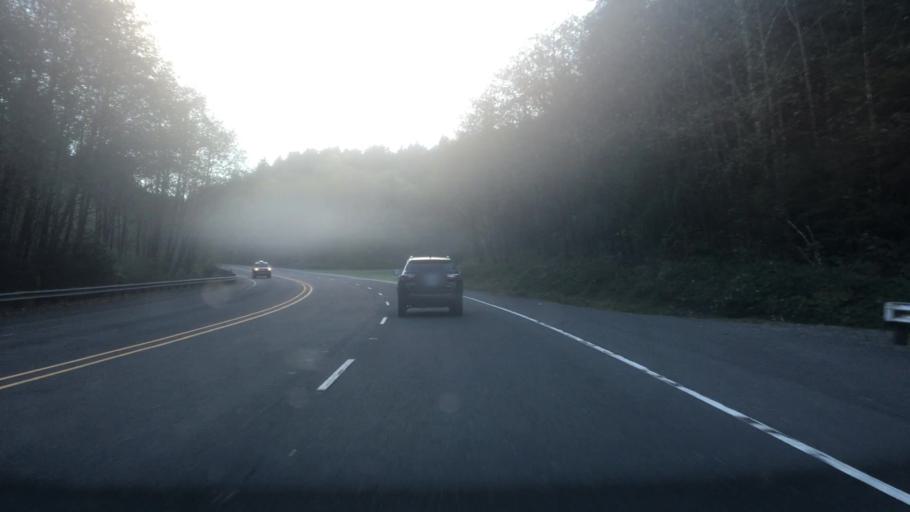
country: US
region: Oregon
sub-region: Clatsop County
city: Cannon Beach
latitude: 45.9203
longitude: -123.9373
